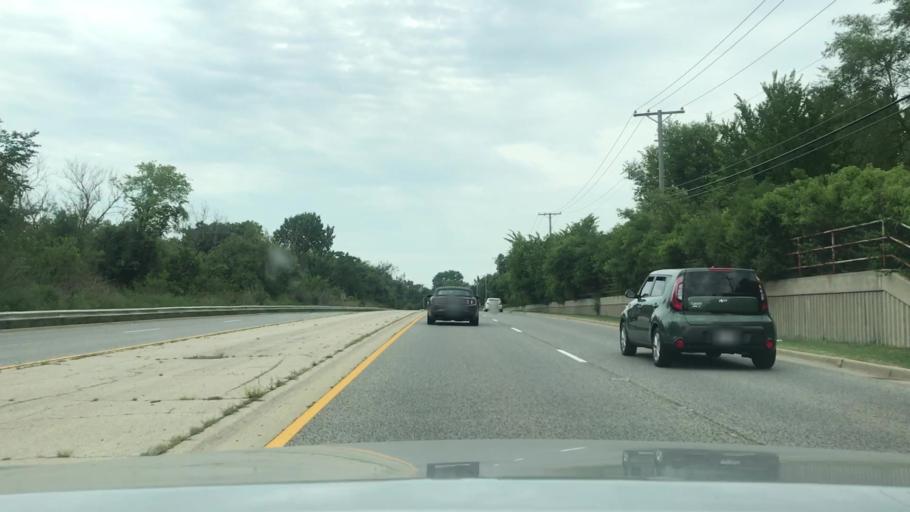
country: US
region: Illinois
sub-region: DuPage County
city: Woodridge
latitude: 41.7440
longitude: -88.0627
